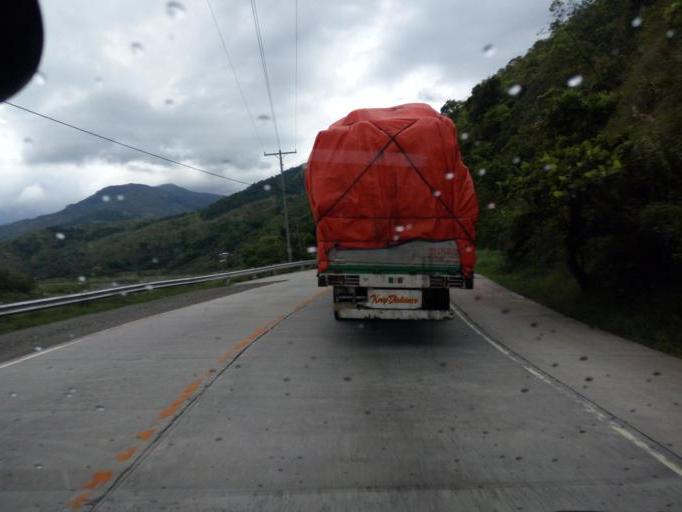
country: PH
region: Central Luzon
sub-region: Province of Nueva Ecija
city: Burgos
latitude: 16.0578
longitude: 120.9493
